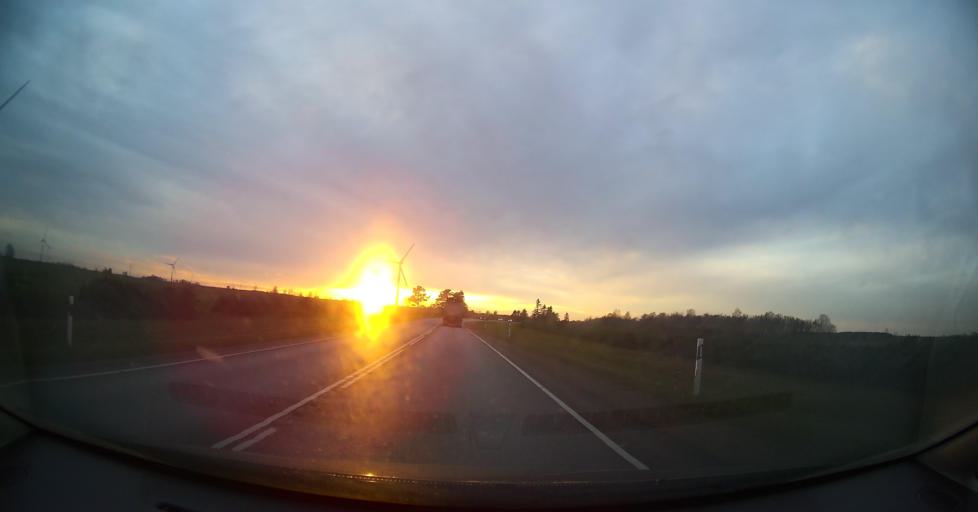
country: EE
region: Ida-Virumaa
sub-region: Aseri vald
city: Aseri
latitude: 59.4456
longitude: 26.7534
